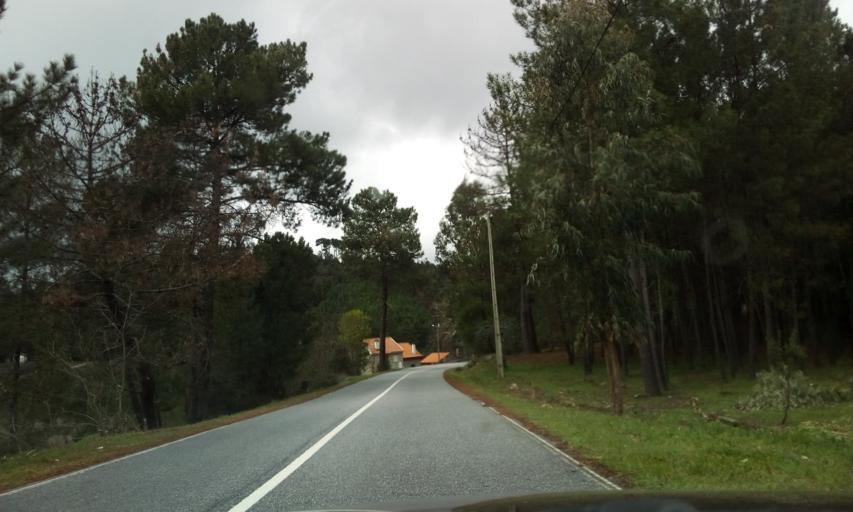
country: PT
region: Guarda
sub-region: Fornos de Algodres
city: Fornos de Algodres
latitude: 40.6084
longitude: -7.5747
